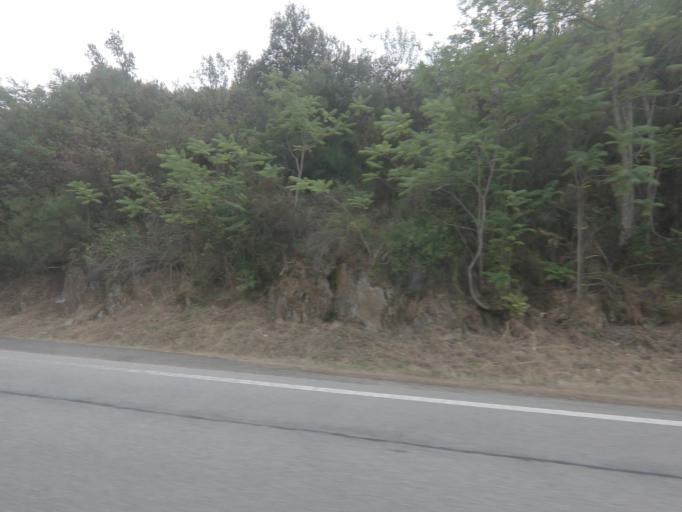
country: PT
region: Viseu
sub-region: Tabuaco
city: Tabuaco
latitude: 41.1584
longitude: -7.5797
